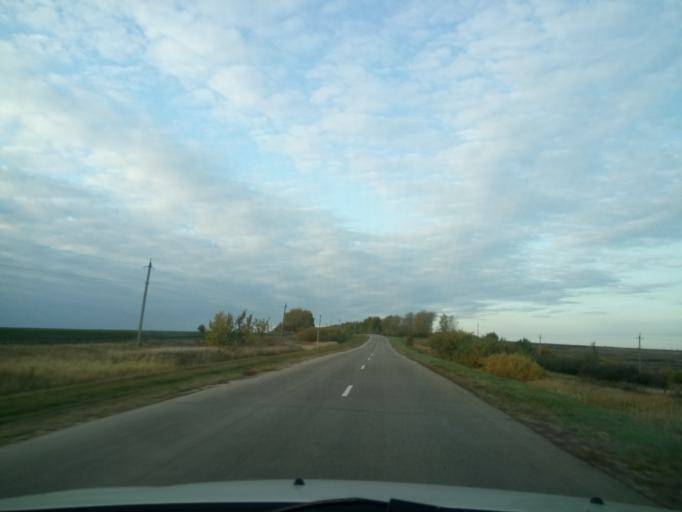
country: RU
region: Nizjnij Novgorod
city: Buturlino
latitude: 55.4827
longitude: 45.0007
